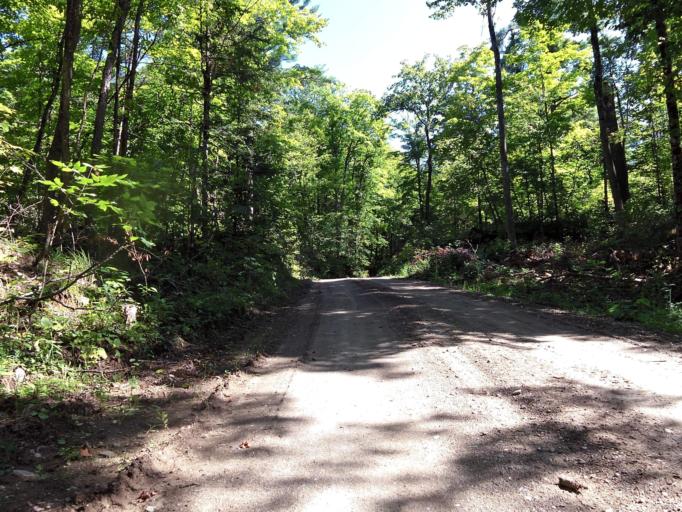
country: CA
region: Ontario
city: Renfrew
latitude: 45.1275
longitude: -76.7196
